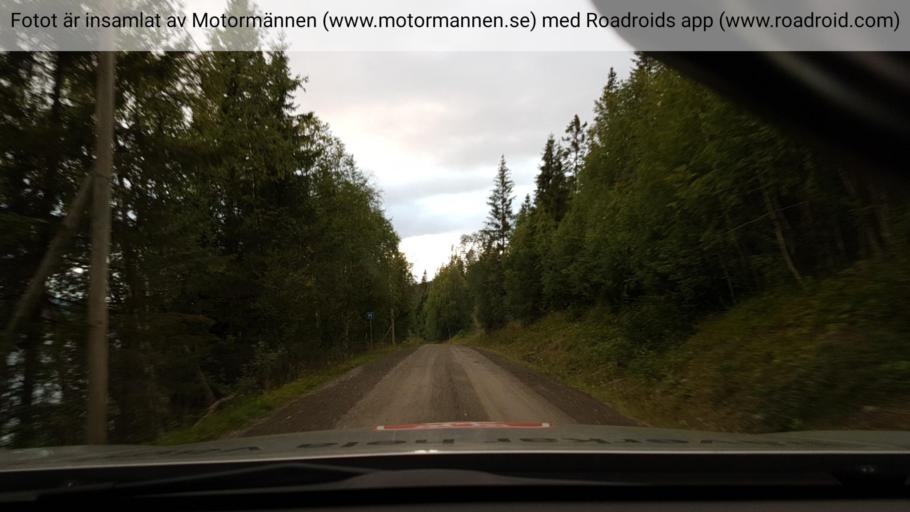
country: NO
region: Nordland
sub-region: Hattfjelldal
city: Hattfjelldal
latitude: 65.6252
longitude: 15.2346
